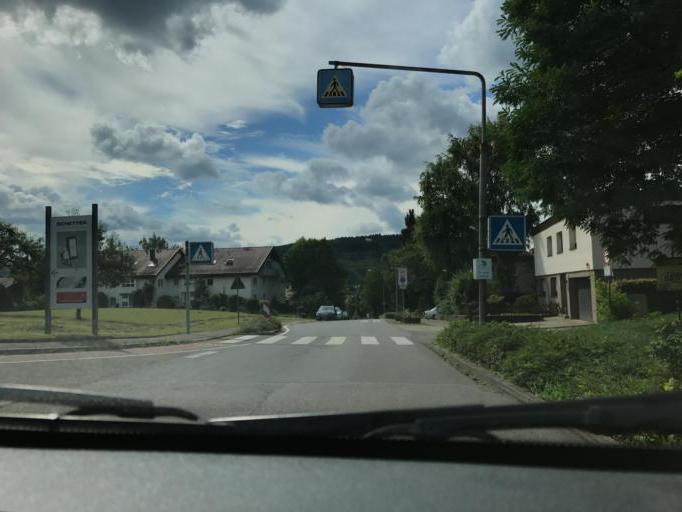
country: DE
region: Baden-Wuerttemberg
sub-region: Regierungsbezirk Stuttgart
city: Weinstadt-Endersbach
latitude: 48.7958
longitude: 9.3390
